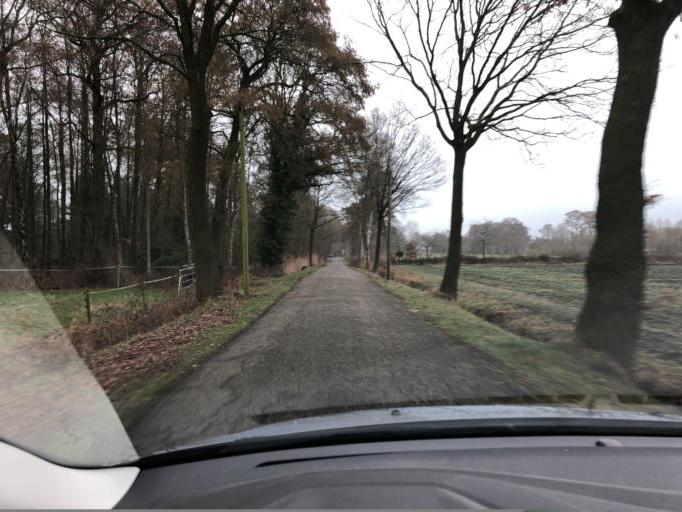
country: DE
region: Lower Saxony
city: Bad Zwischenahn
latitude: 53.1755
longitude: 8.0378
